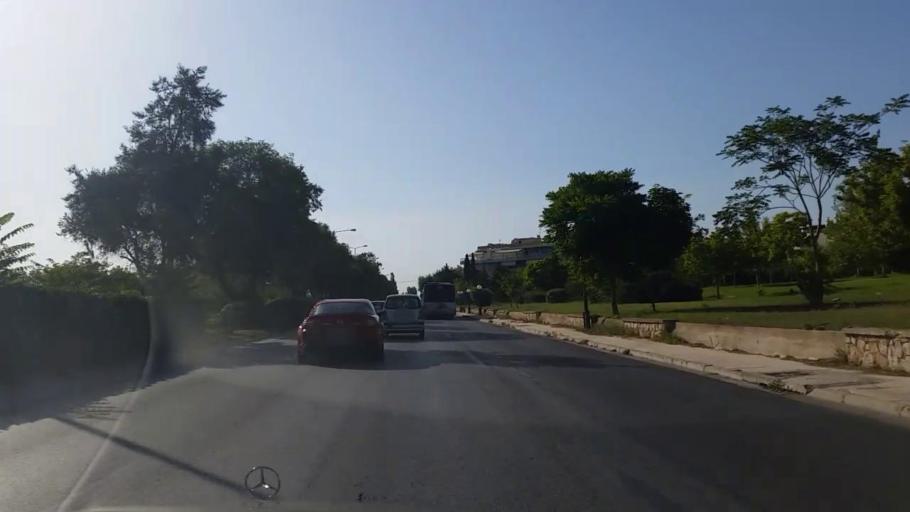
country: GR
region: Attica
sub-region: Nomarchia Anatolikis Attikis
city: Voula
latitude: 37.8424
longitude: 23.7586
